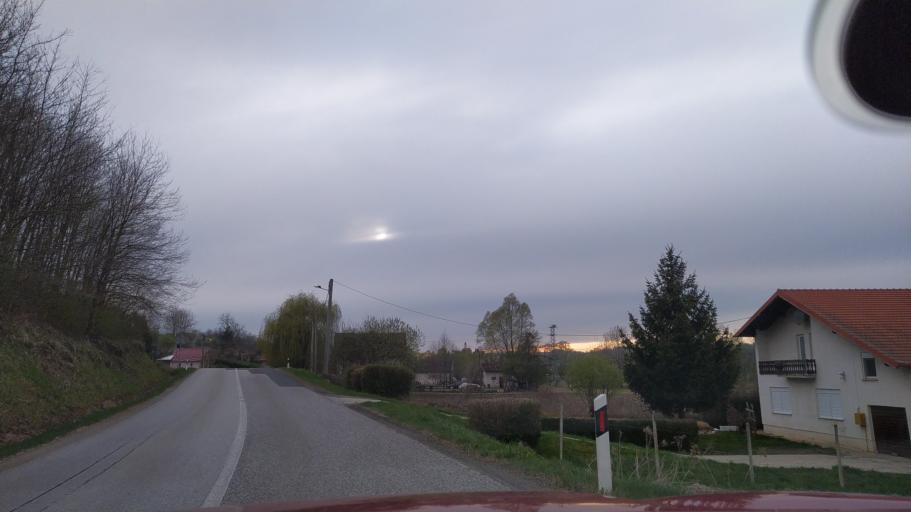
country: HR
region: Varazdinska
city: Jalzabet
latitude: 46.2116
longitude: 16.5000
